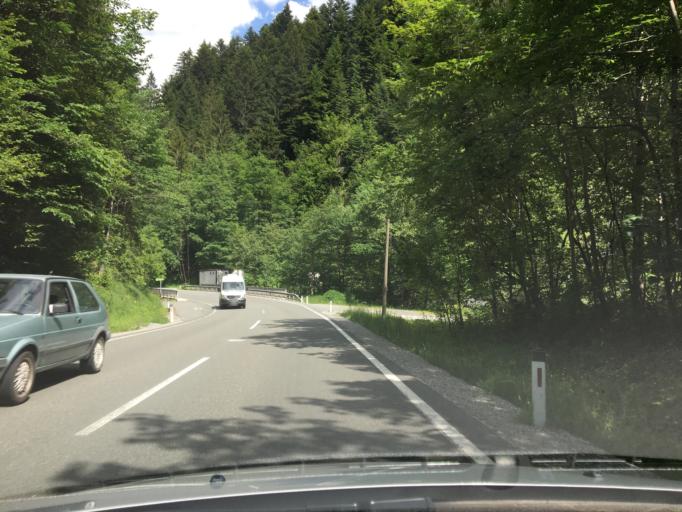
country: AT
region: Salzburg
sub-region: Politischer Bezirk Sankt Johann im Pongau
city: Sankt Johann im Pongau
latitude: 47.3316
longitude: 13.2380
